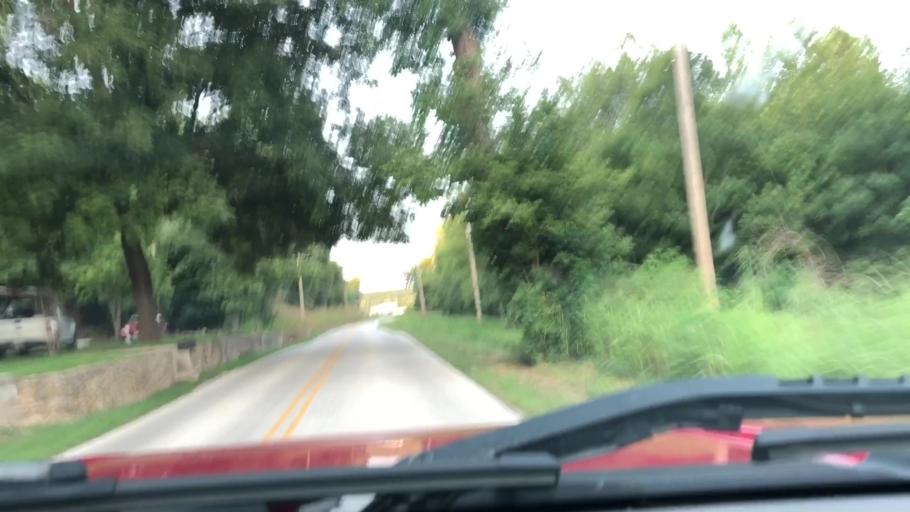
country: US
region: Missouri
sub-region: Jasper County
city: Duquesne
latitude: 37.0176
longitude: -94.4869
